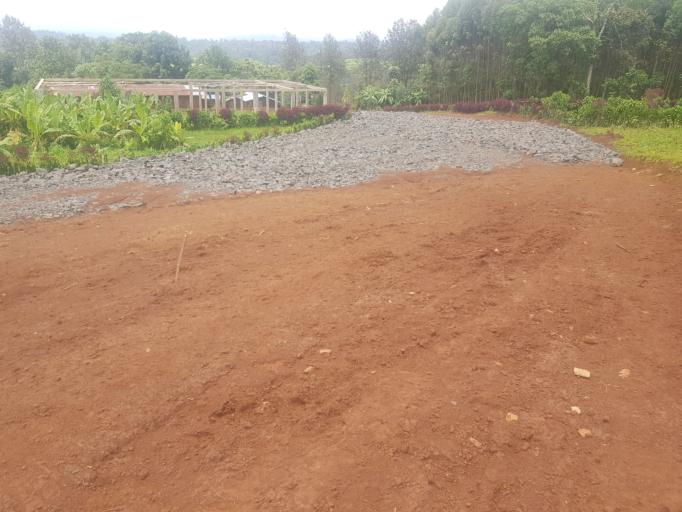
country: ET
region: Oromiya
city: Gore
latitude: 7.8356
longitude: 35.4708
